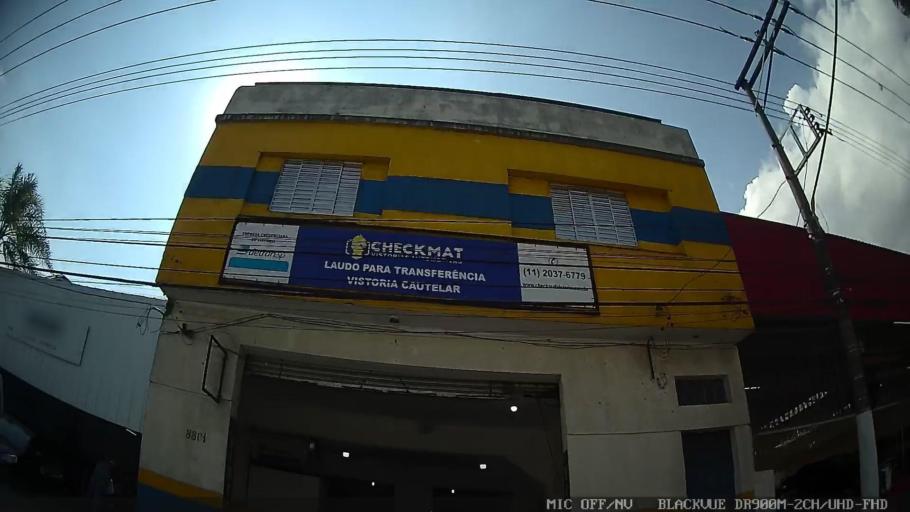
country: BR
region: Sao Paulo
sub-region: Guarulhos
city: Guarulhos
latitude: -23.4961
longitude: -46.4528
